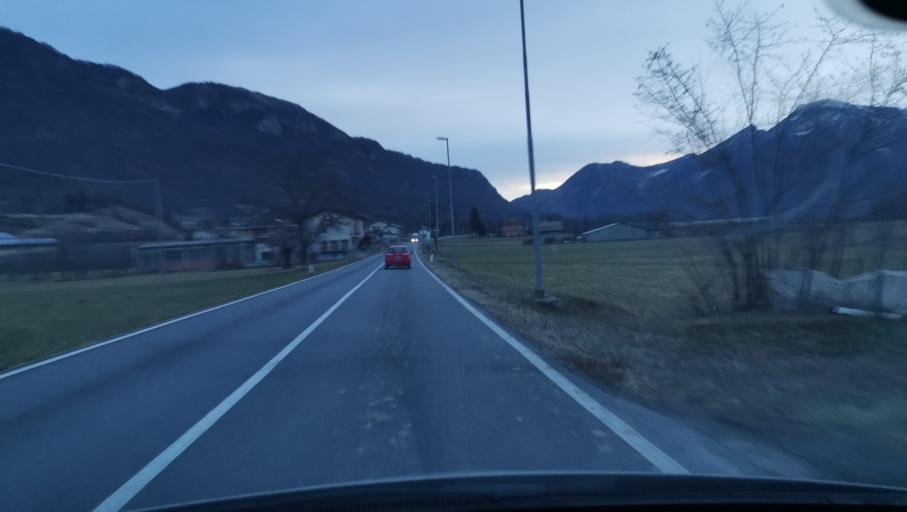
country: IT
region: Piedmont
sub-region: Provincia di Cuneo
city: Demonte
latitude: 44.3165
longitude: 7.3085
